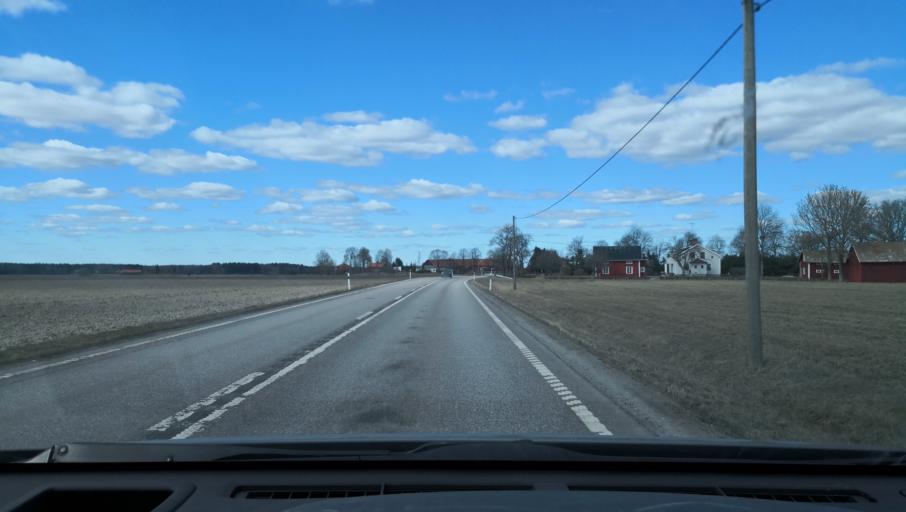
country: SE
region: Vaestmanland
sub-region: Sala Kommun
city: Sala
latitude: 59.8616
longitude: 16.6322
